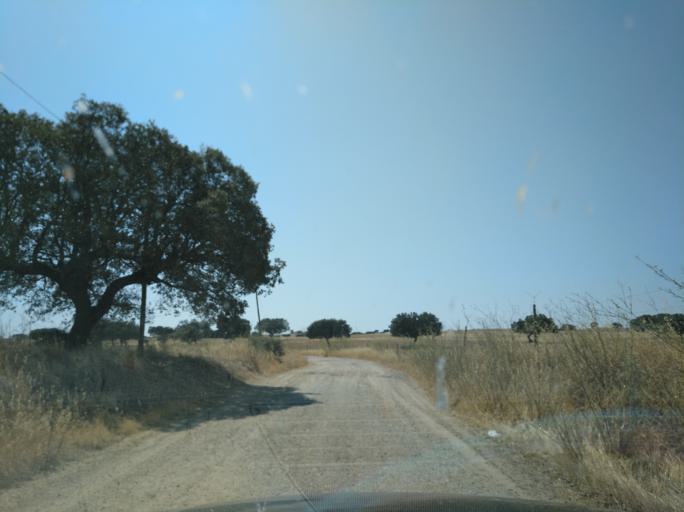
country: PT
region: Portalegre
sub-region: Campo Maior
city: Campo Maior
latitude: 39.0333
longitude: -6.9834
